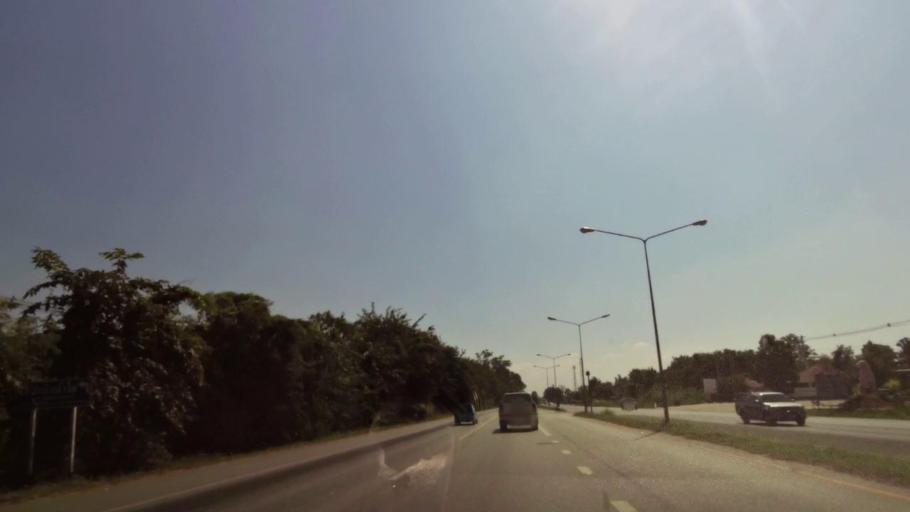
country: TH
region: Nakhon Sawan
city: Kao Liao
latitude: 15.8130
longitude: 100.1201
